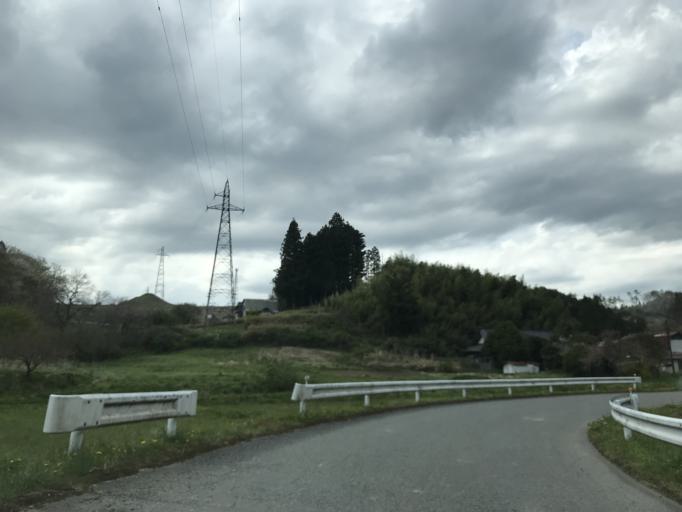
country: JP
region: Iwate
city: Ichinoseki
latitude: 38.7910
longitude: 141.4228
